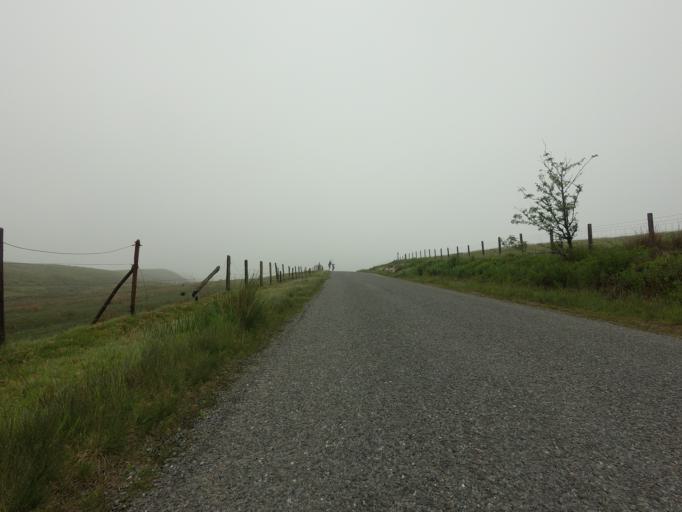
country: GB
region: Scotland
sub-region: Perth and Kinross
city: Kinross
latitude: 56.1534
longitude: -3.4535
